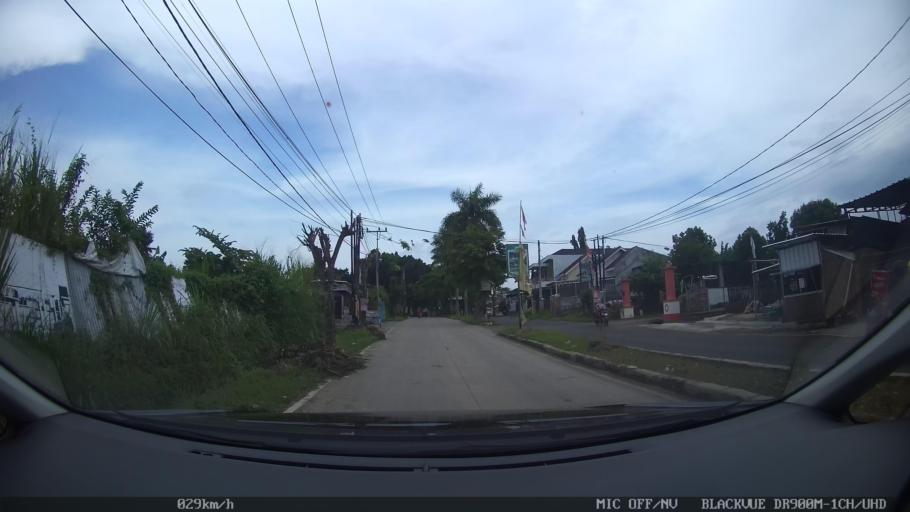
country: ID
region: Lampung
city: Kedaton
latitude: -5.3782
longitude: 105.2119
